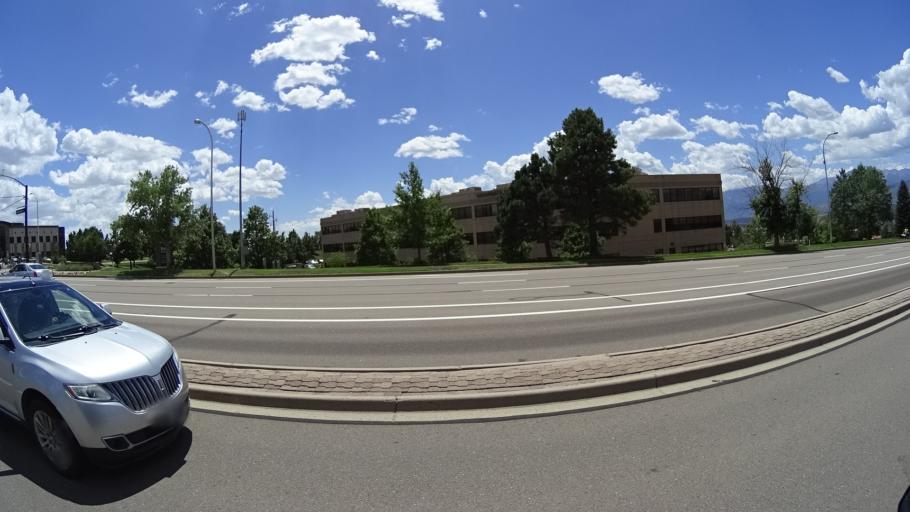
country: US
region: Colorado
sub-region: El Paso County
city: Air Force Academy
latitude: 38.9608
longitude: -104.7850
